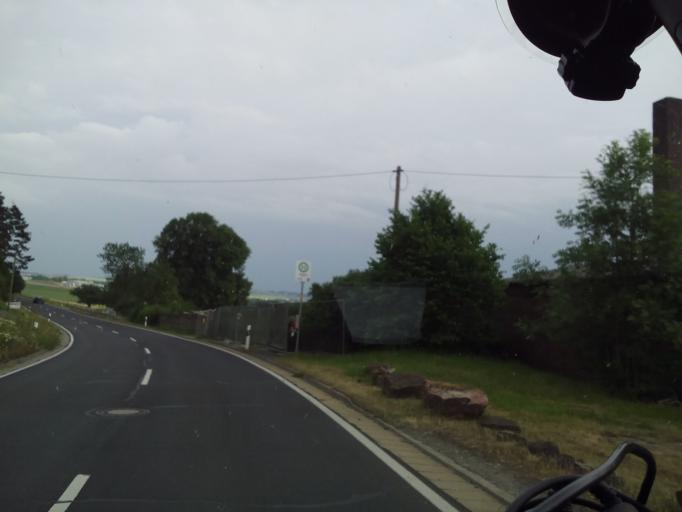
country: DE
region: Bavaria
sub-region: Regierungsbezirk Unterfranken
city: Stockheim
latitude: 50.4510
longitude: 10.2826
